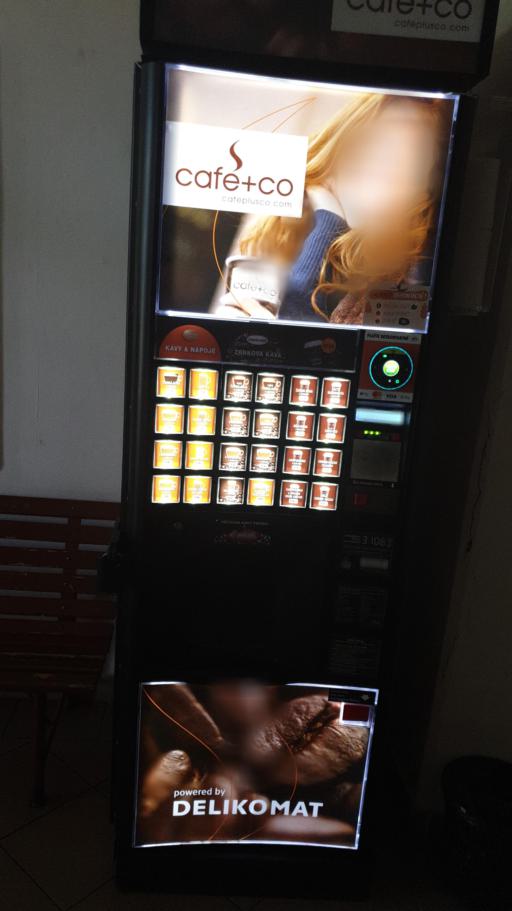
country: CZ
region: Ustecky
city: Ceska Kamenice
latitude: 50.7959
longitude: 14.4139
